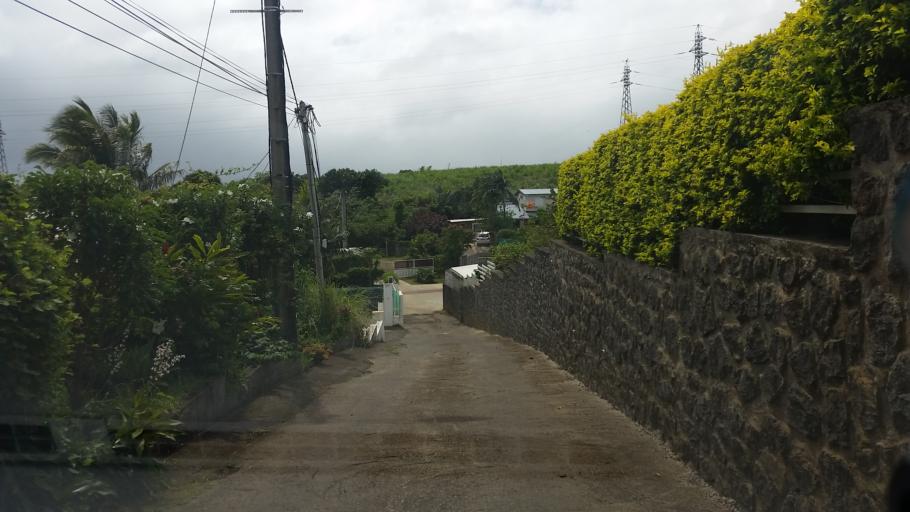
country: RE
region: Reunion
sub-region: Reunion
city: Sainte-Marie
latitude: -20.9214
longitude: 55.5323
